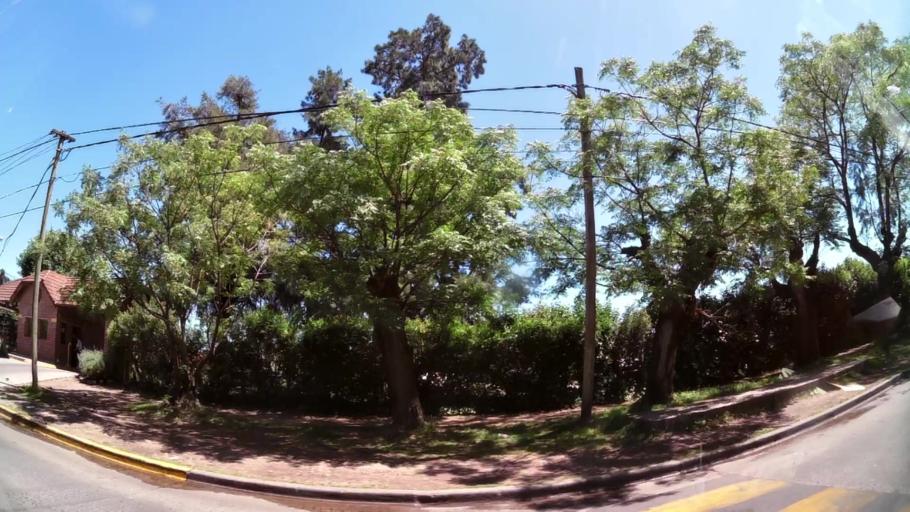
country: AR
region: Buenos Aires
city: Hurlingham
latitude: -34.4974
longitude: -58.6423
